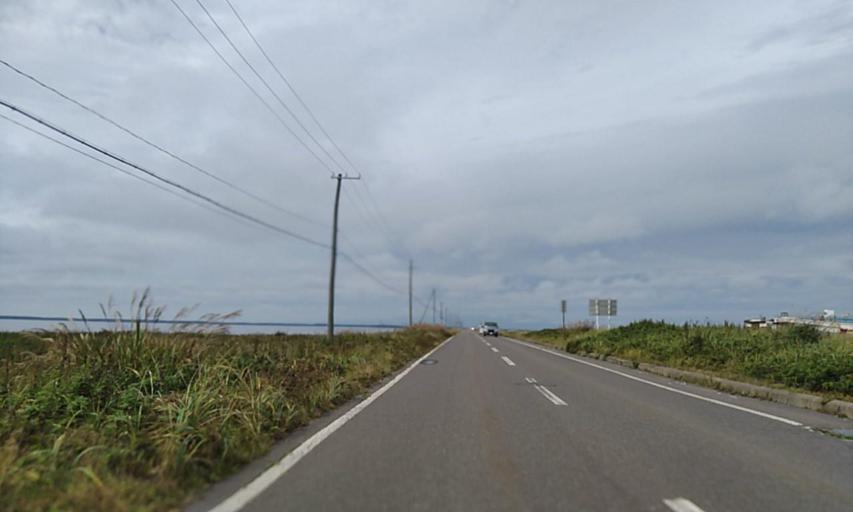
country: JP
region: Hokkaido
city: Shibetsu
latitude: 43.6104
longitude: 145.2692
